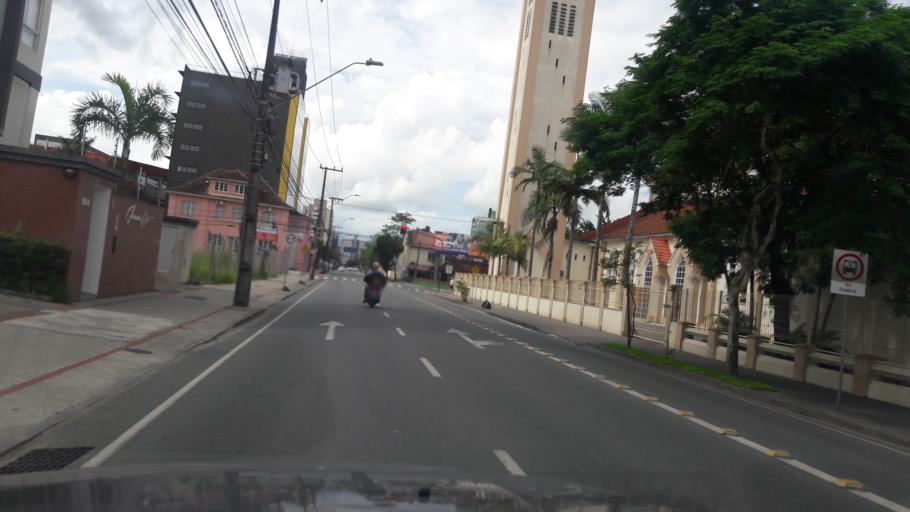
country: BR
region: Santa Catarina
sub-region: Joinville
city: Joinville
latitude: -26.3171
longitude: -48.8426
